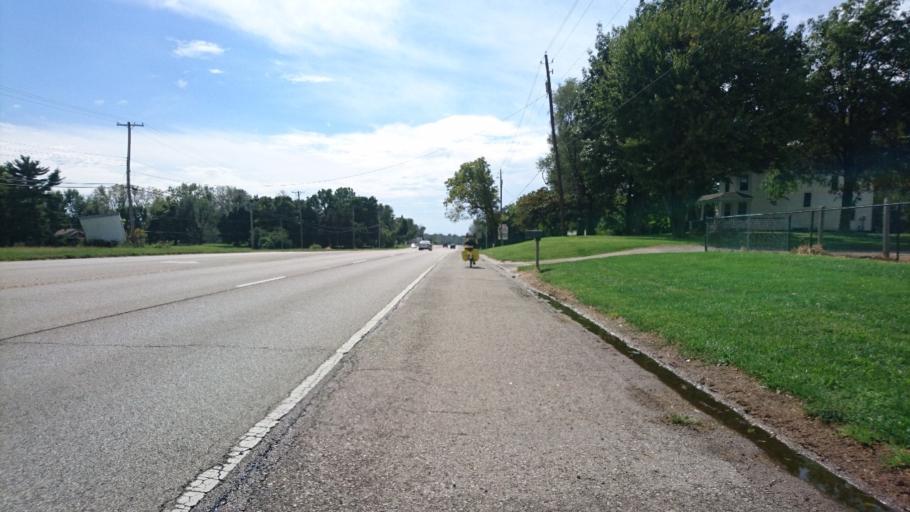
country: US
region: Illinois
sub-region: Sangamon County
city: Grandview
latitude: 39.8519
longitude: -89.6234
